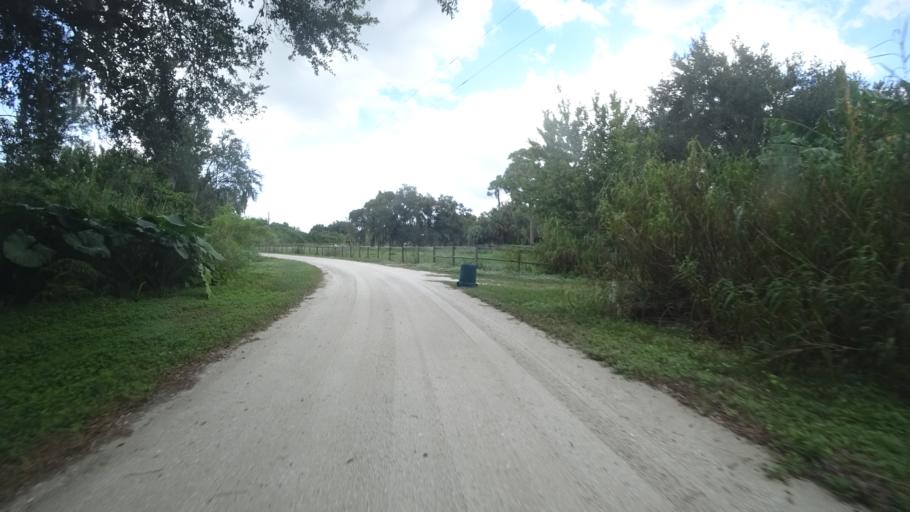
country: US
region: Florida
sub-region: Manatee County
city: Memphis
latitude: 27.6183
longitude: -82.5145
